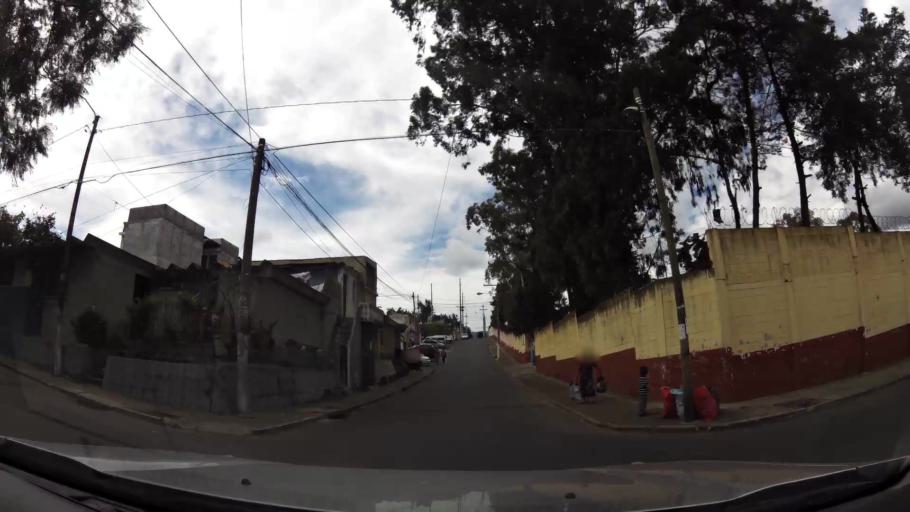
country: GT
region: Guatemala
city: Mixco
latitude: 14.6700
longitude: -90.5663
